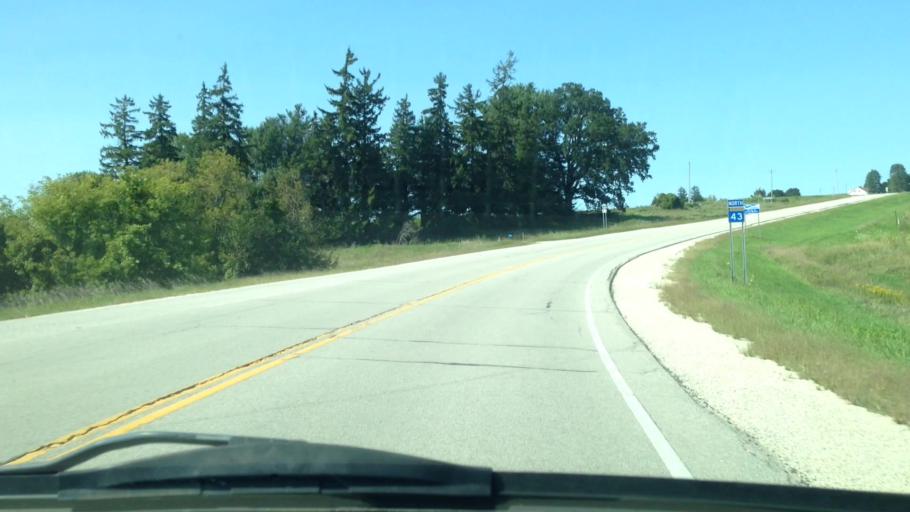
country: US
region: Minnesota
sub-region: Houston County
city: Spring Grove
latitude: 43.6029
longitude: -91.7896
